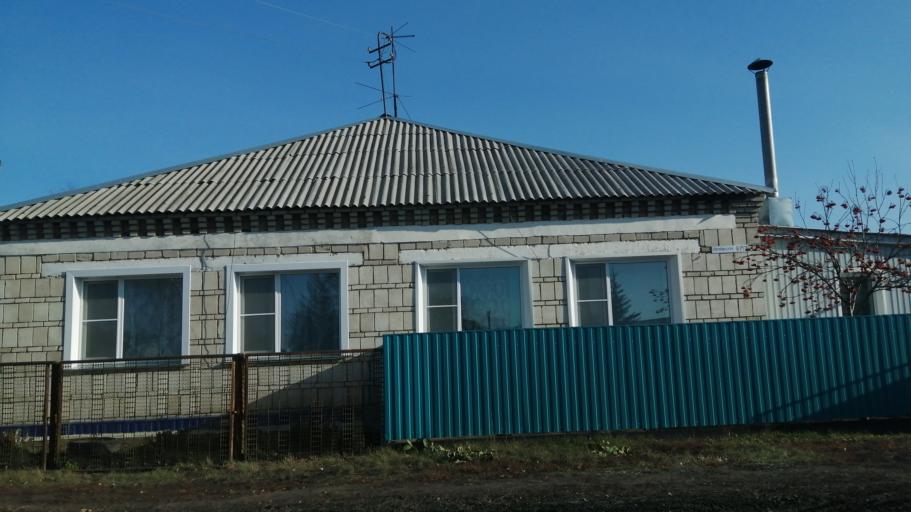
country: RU
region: Novosibirsk
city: Krasnozerskoye
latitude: 53.9745
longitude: 79.2461
